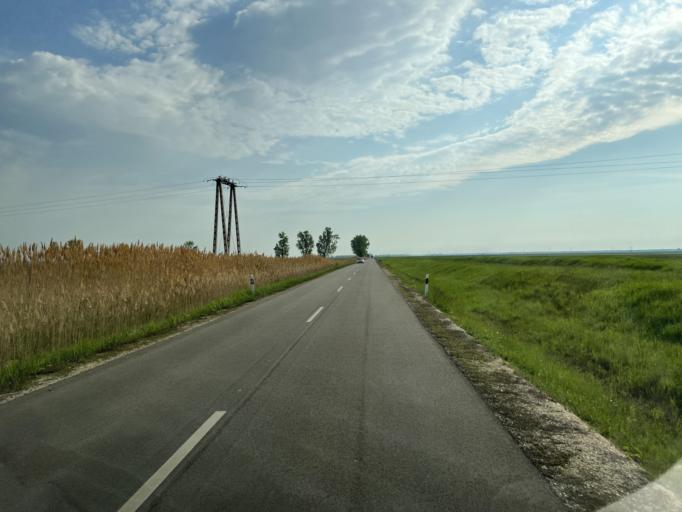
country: HU
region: Pest
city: Jaszkarajeno
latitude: 47.1015
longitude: 20.0297
